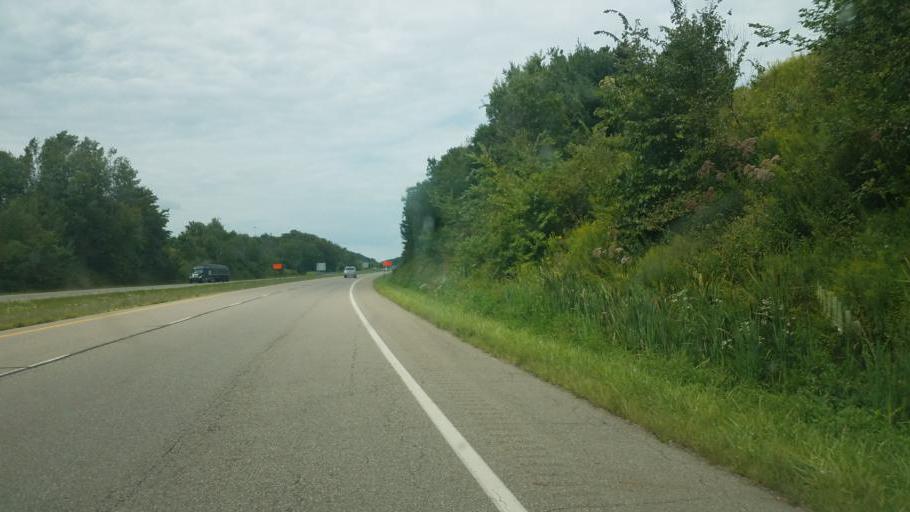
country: US
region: Ohio
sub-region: Columbiana County
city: Lisbon
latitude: 40.7708
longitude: -80.7317
